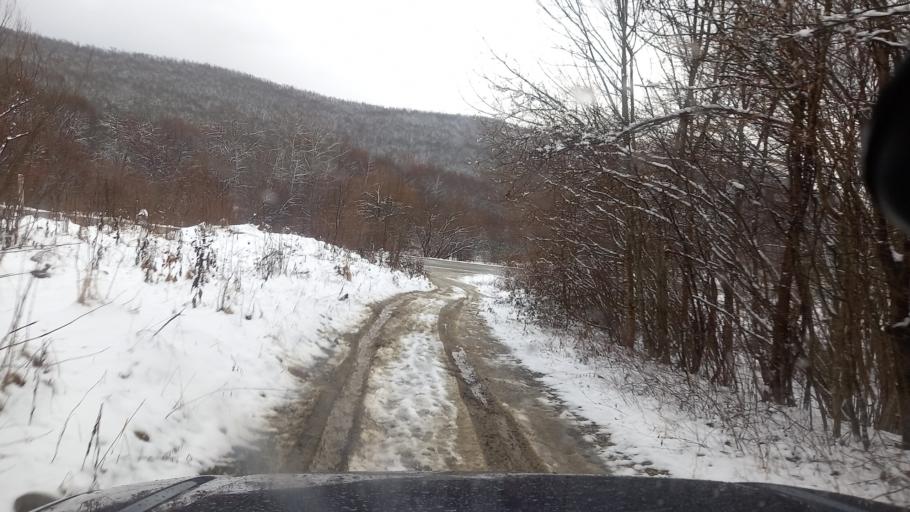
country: RU
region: Adygeya
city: Abadzekhskaya
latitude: 44.3711
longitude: 40.2589
